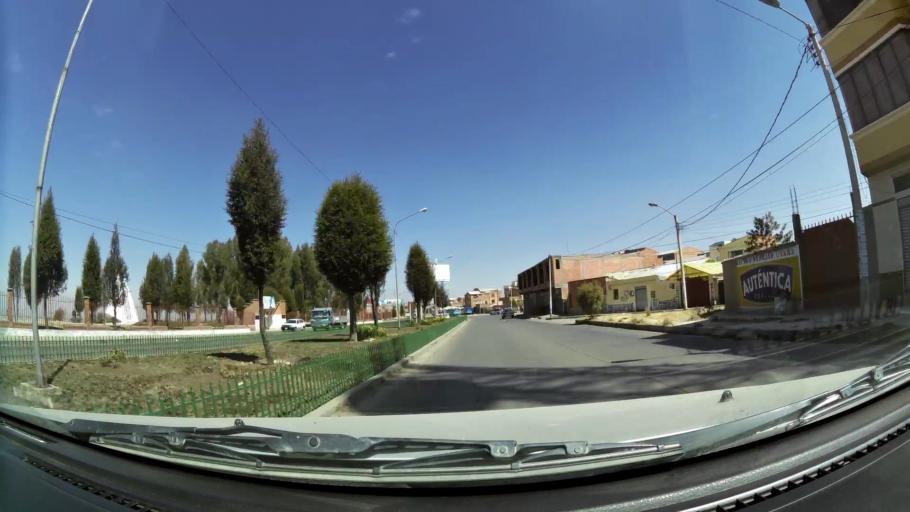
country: BO
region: La Paz
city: La Paz
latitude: -16.5294
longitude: -68.1464
